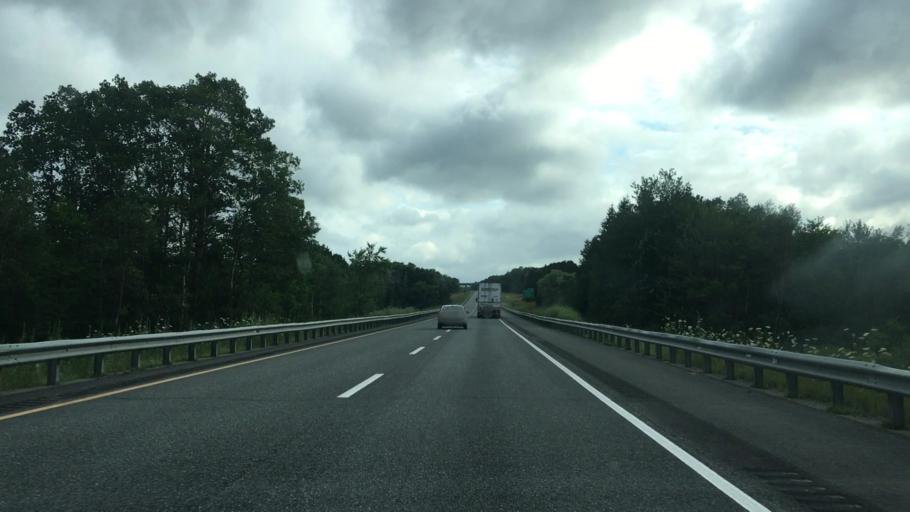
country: US
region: Maine
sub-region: Kennebec County
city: Clinton
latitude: 44.6551
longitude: -69.5089
